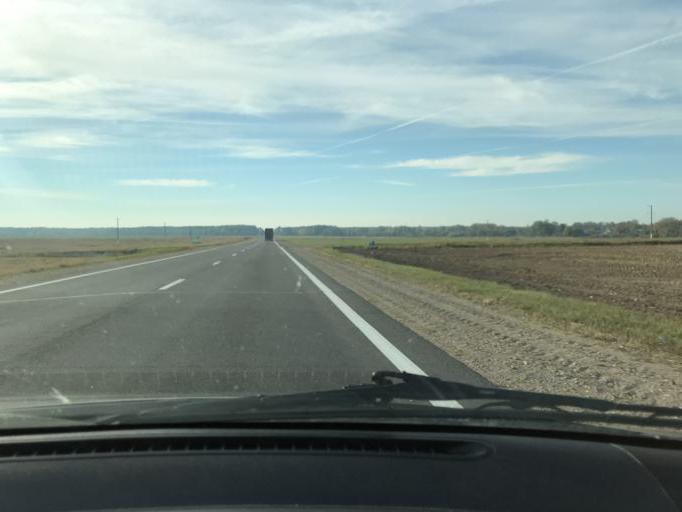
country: BY
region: Brest
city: Horad Pinsk
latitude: 52.1495
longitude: 25.8721
